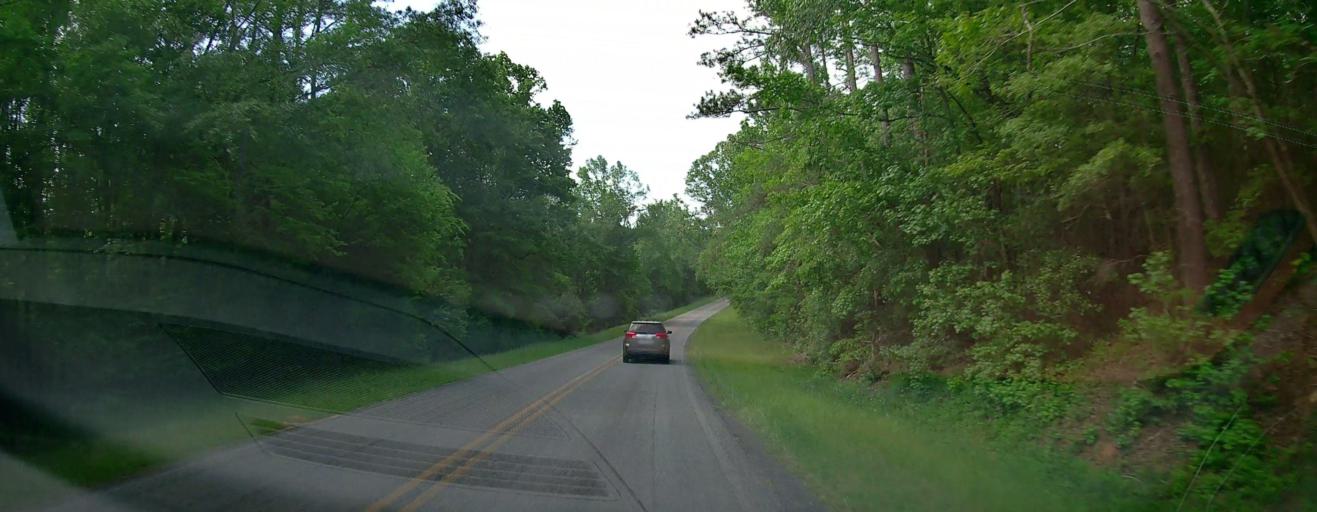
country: US
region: Georgia
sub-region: Laurens County
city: East Dublin
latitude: 32.6696
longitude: -82.8953
